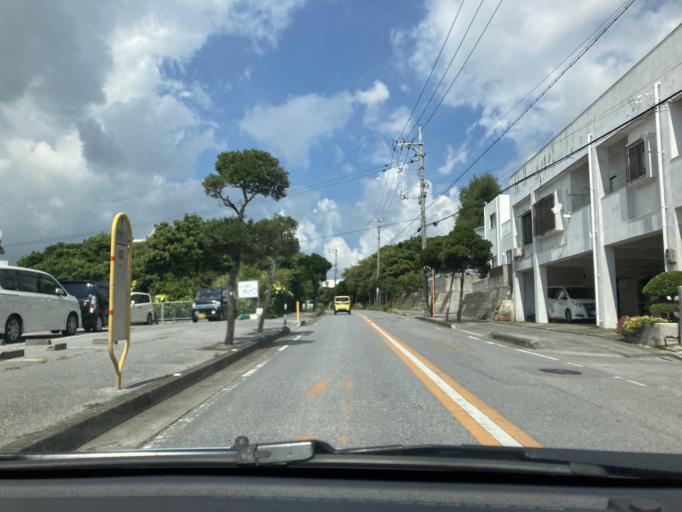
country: JP
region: Okinawa
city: Tomigusuku
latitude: 26.1474
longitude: 127.7622
